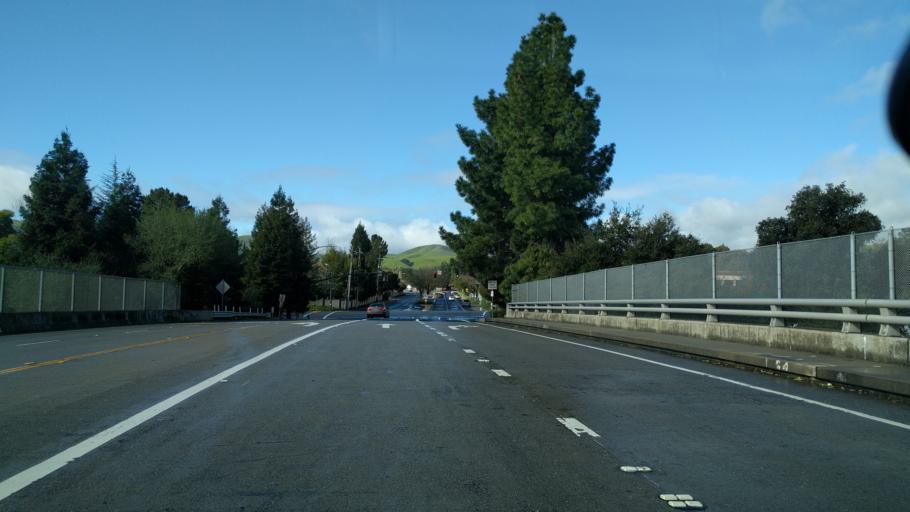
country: US
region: California
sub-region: Contra Costa County
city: San Ramon
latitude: 37.7716
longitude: -121.9723
